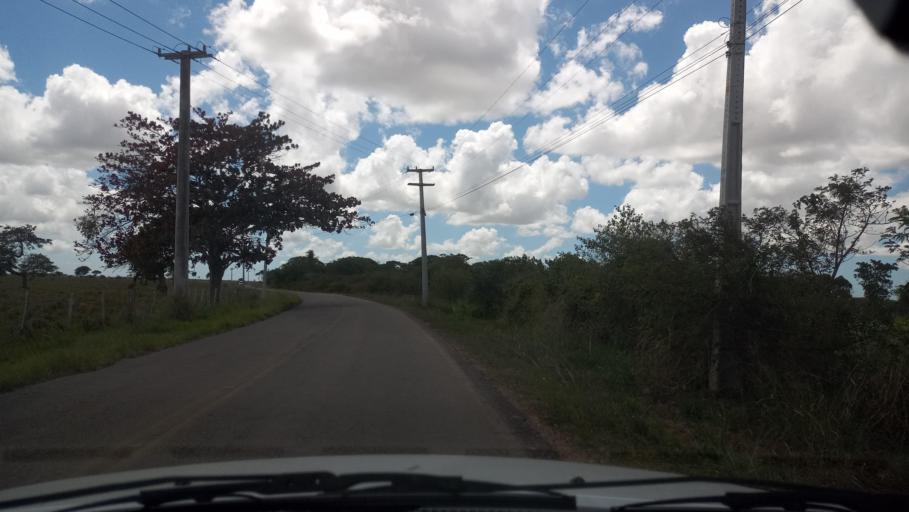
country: BR
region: Rio Grande do Norte
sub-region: Brejinho
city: Brejinho
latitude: -6.0418
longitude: -35.4065
